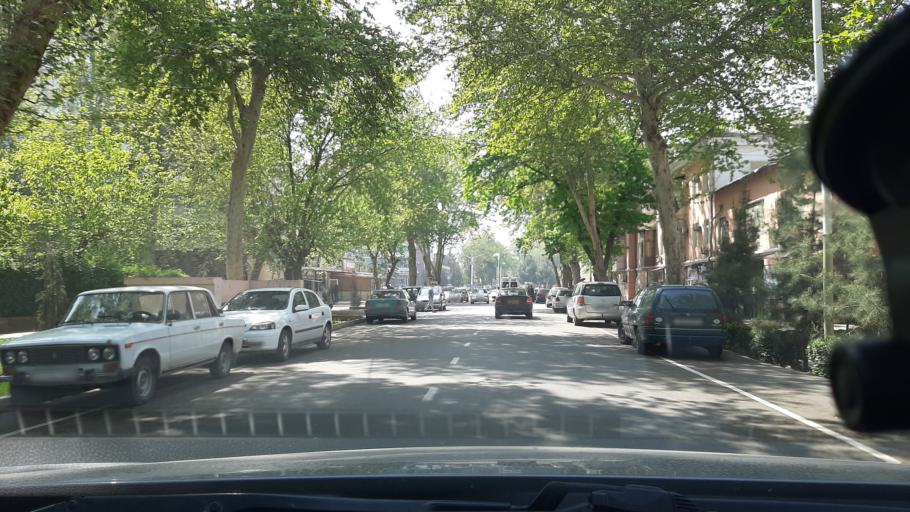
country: TJ
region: Viloyati Sughd
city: Khujand
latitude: 40.2842
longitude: 69.6254
